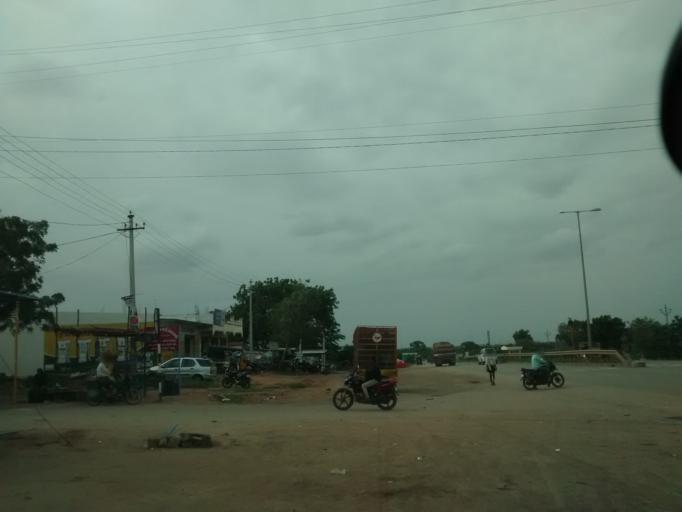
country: IN
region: Telangana
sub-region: Mahbubnagar
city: Gadwal
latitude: 16.1131
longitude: 77.8861
